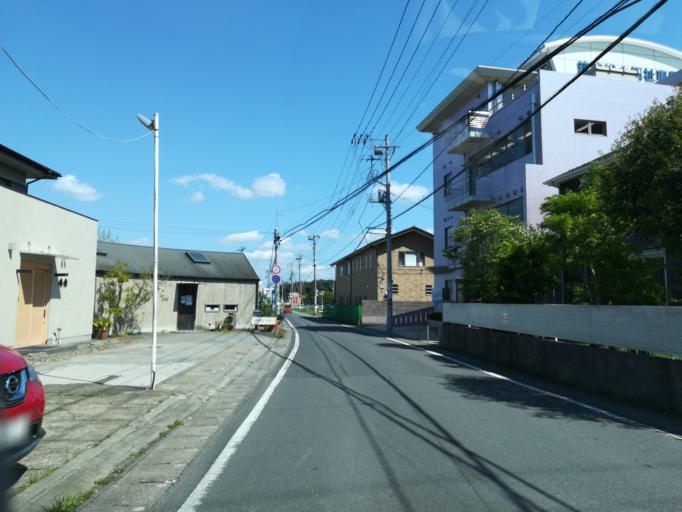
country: JP
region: Ibaraki
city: Naka
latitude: 36.0757
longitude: 140.1051
